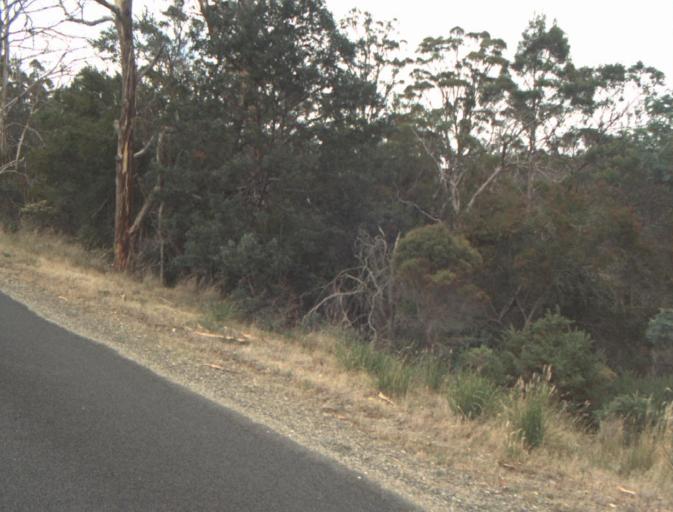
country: AU
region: Tasmania
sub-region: Northern Midlands
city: Evandale
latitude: -41.4951
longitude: 147.3885
